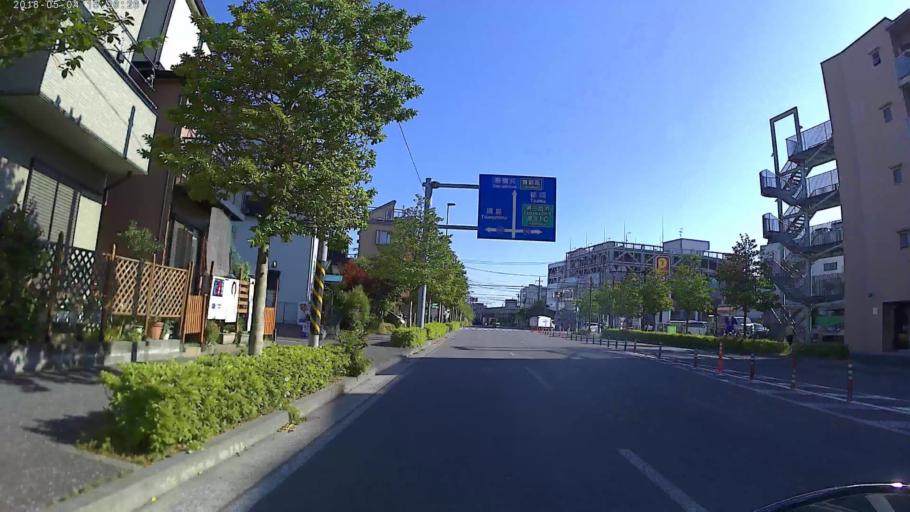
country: JP
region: Kanagawa
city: Yokohama
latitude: 35.5291
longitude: 139.6130
